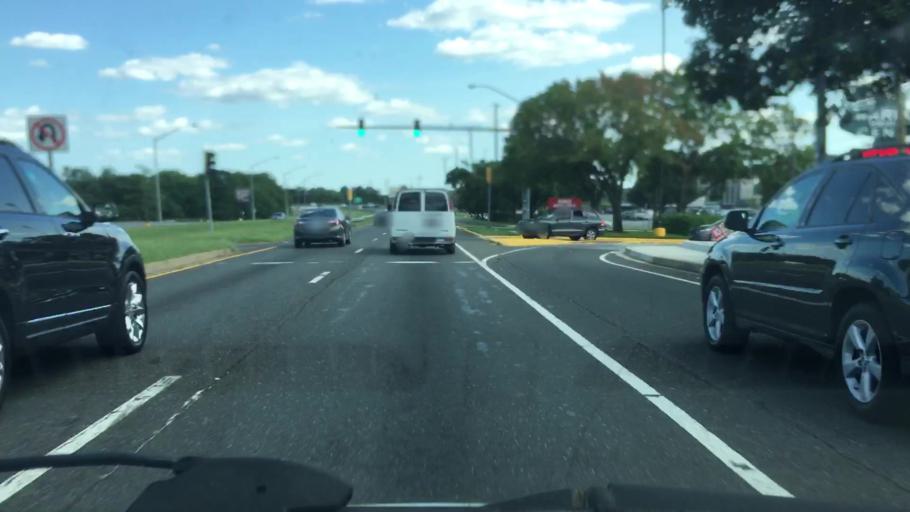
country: US
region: Maryland
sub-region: Prince George's County
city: Silver Hill
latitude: 38.8363
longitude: -76.9442
